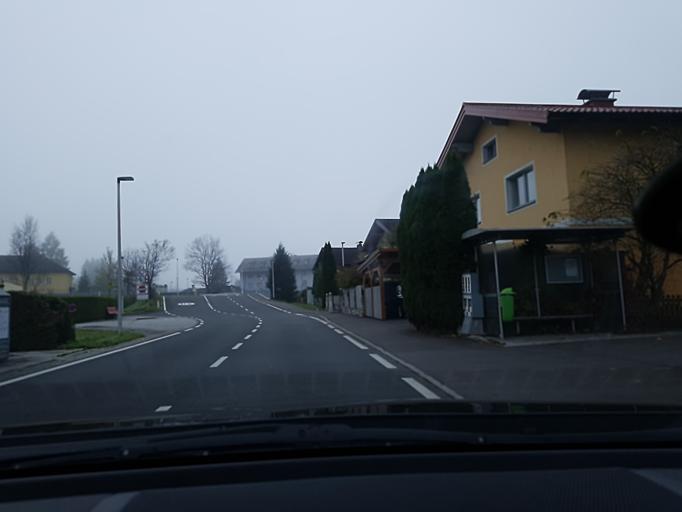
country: AT
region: Salzburg
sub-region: Politischer Bezirk Sankt Johann im Pongau
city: Sankt Johann im Pongau
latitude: 47.3559
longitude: 13.2053
